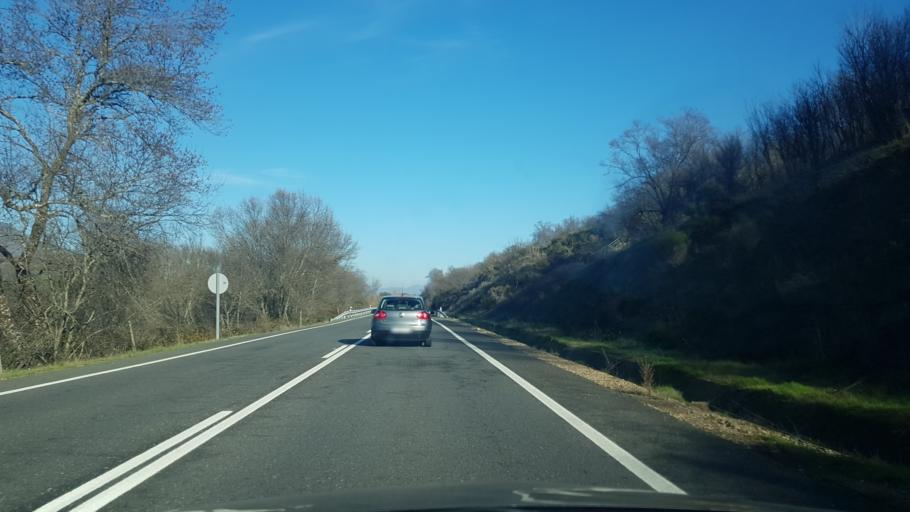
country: ES
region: Castille and Leon
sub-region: Provincia de Avila
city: Navahondilla
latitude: 40.3173
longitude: -4.4949
